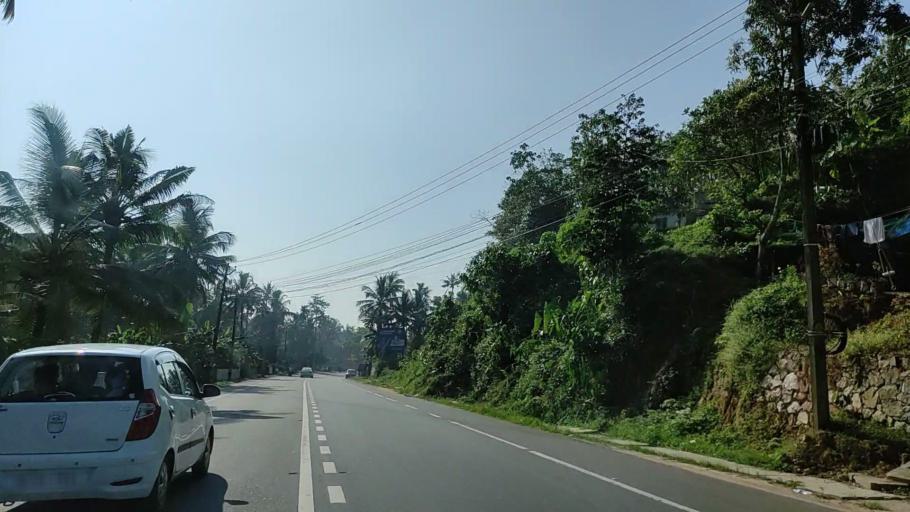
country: IN
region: Kerala
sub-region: Kollam
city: Punalur
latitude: 8.9208
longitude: 76.8547
